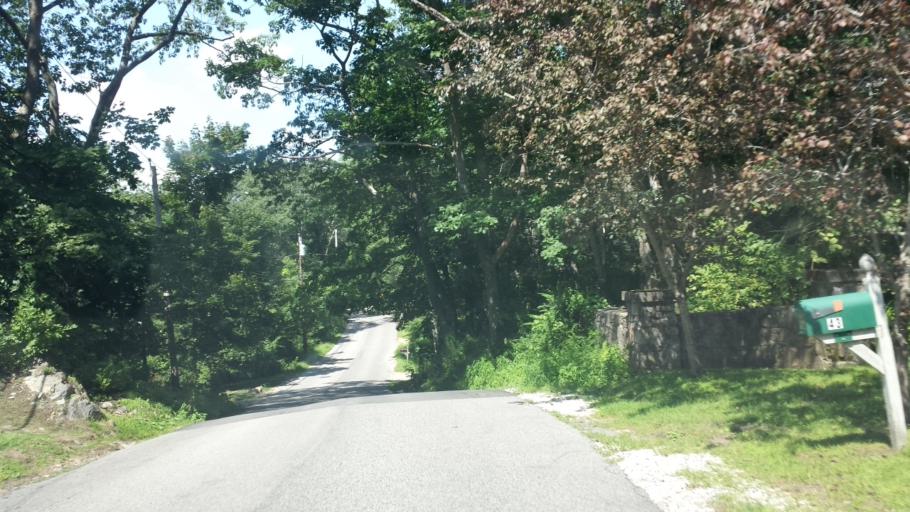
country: US
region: Maine
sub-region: York County
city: Kennebunkport
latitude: 43.3512
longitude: -70.4698
